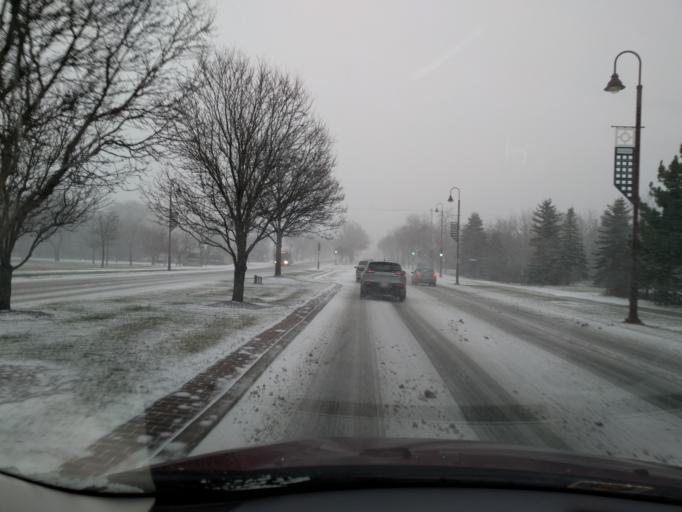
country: US
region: Wisconsin
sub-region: Milwaukee County
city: Glendale
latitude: 43.1190
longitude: -87.9412
